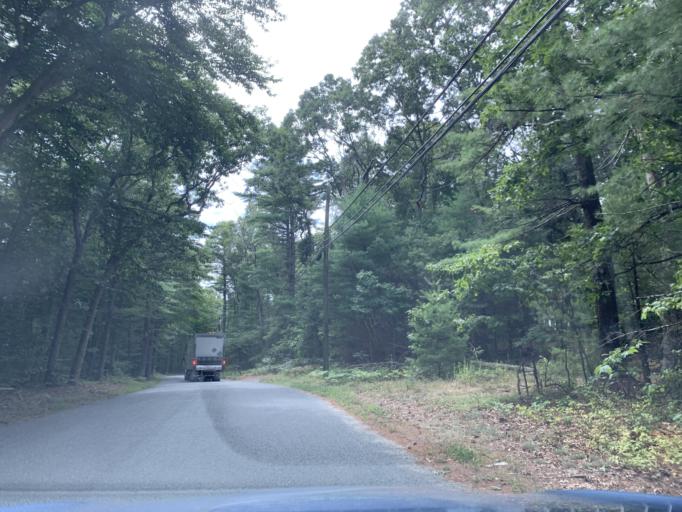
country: US
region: Rhode Island
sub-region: Kent County
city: West Greenwich
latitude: 41.5773
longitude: -71.6215
